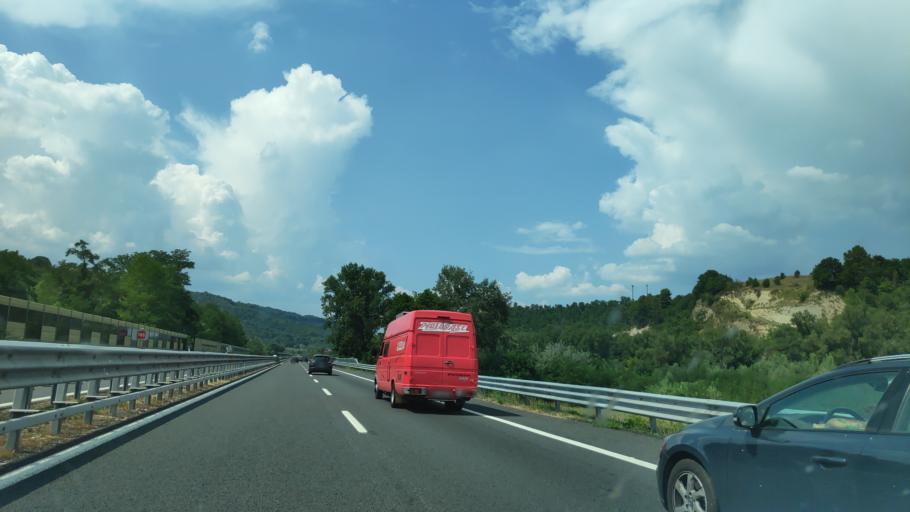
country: IT
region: Umbria
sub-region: Provincia di Terni
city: Orvieto Scalo
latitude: 42.7014
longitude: 12.1742
